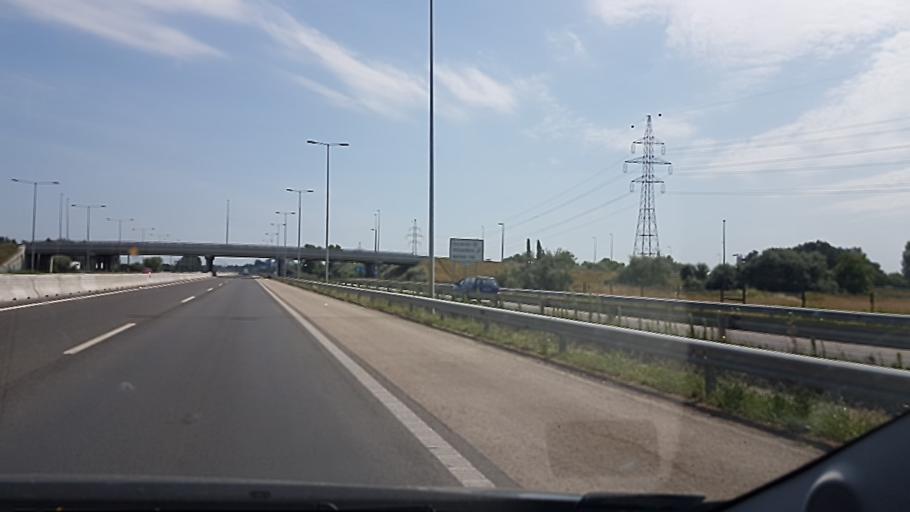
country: HU
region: Budapest
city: Budapest XIX. keruelet
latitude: 47.4265
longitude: 19.1510
